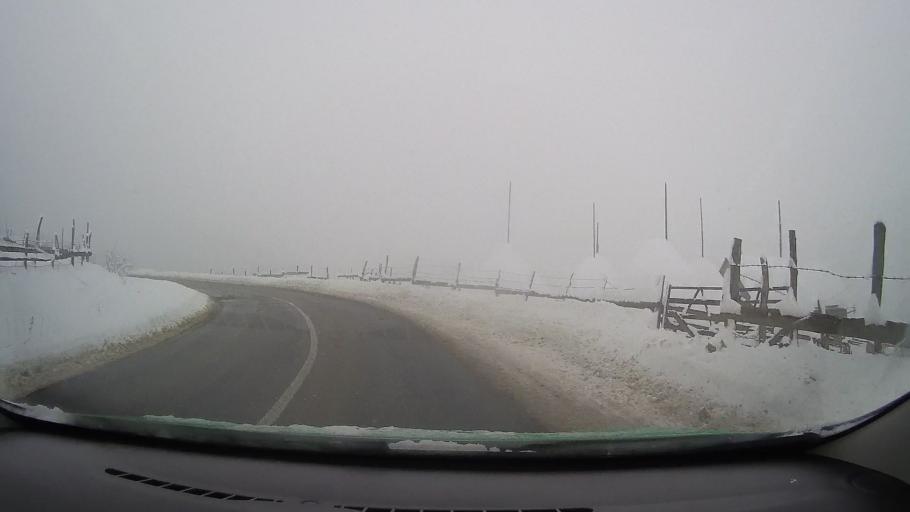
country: RO
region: Sibiu
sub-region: Comuna Jina
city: Jina
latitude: 45.7877
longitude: 23.6991
